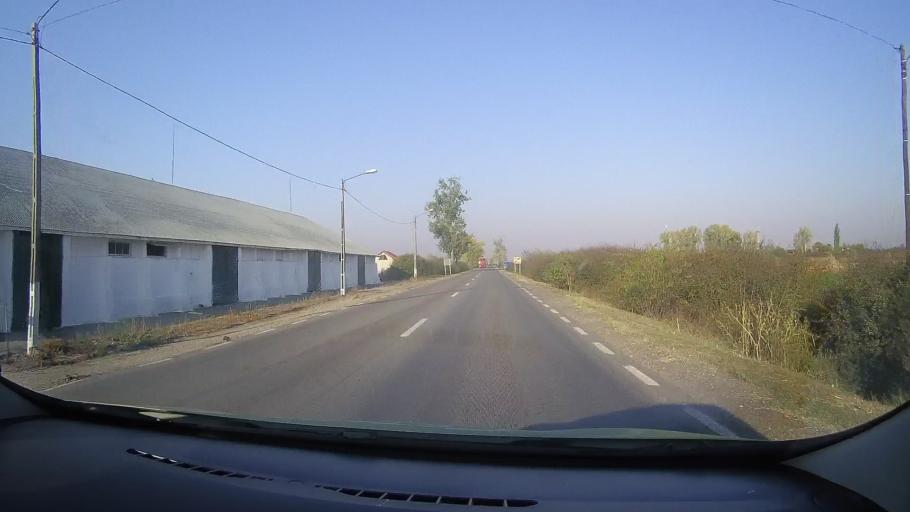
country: RO
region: Arad
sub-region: Comuna Socodor
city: Socodor
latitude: 46.5016
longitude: 21.4289
